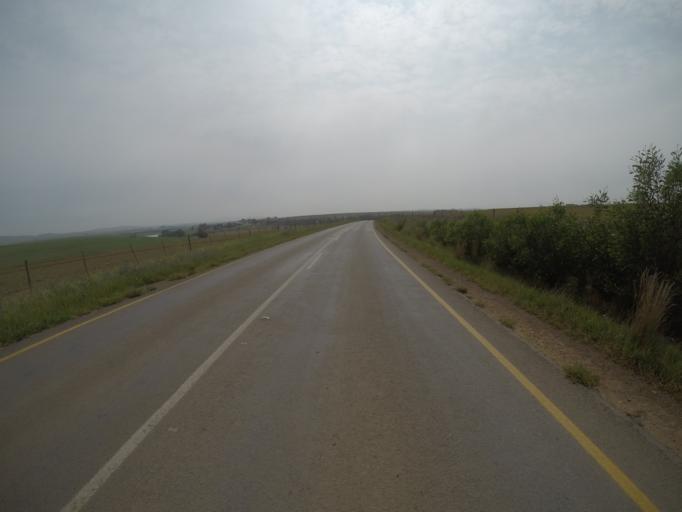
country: ZA
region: Western Cape
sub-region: City of Cape Town
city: Kraaifontein
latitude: -33.7355
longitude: 18.6337
